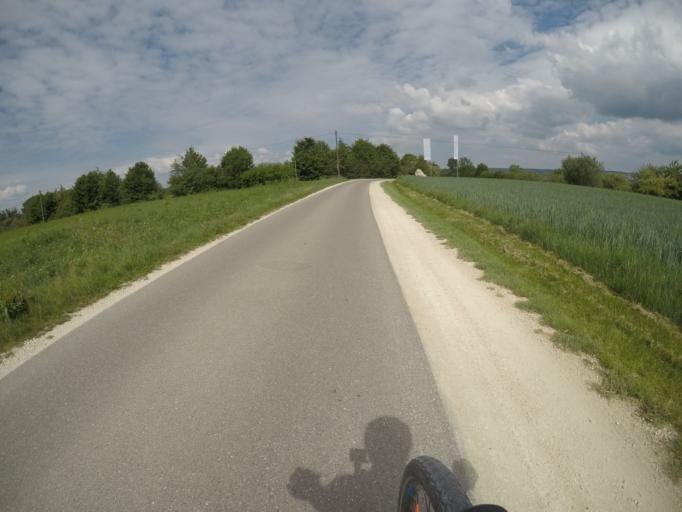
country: DE
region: Baden-Wuerttemberg
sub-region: Regierungsbezirk Stuttgart
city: Notzingen
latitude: 48.6687
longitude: 9.4292
